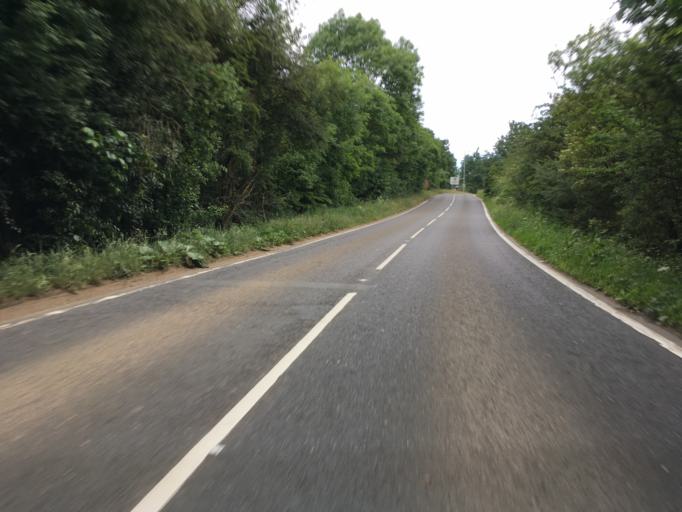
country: GB
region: England
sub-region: Central Bedfordshire
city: Potsgrove
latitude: 51.9609
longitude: -0.6427
